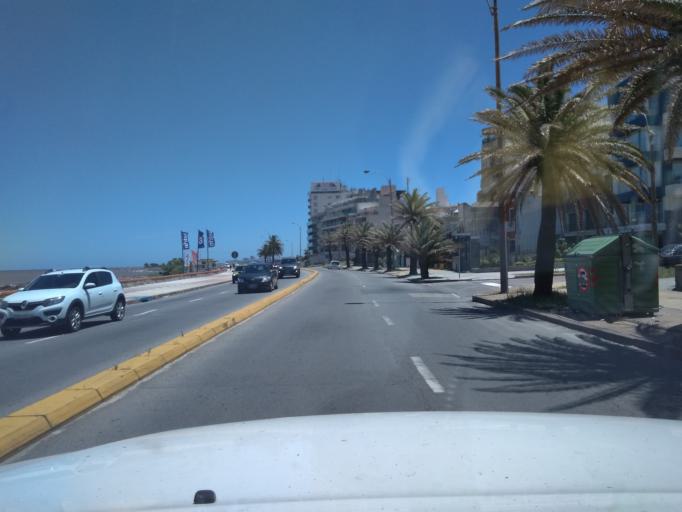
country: UY
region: Canelones
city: Paso de Carrasco
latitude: -34.8957
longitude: -56.0940
